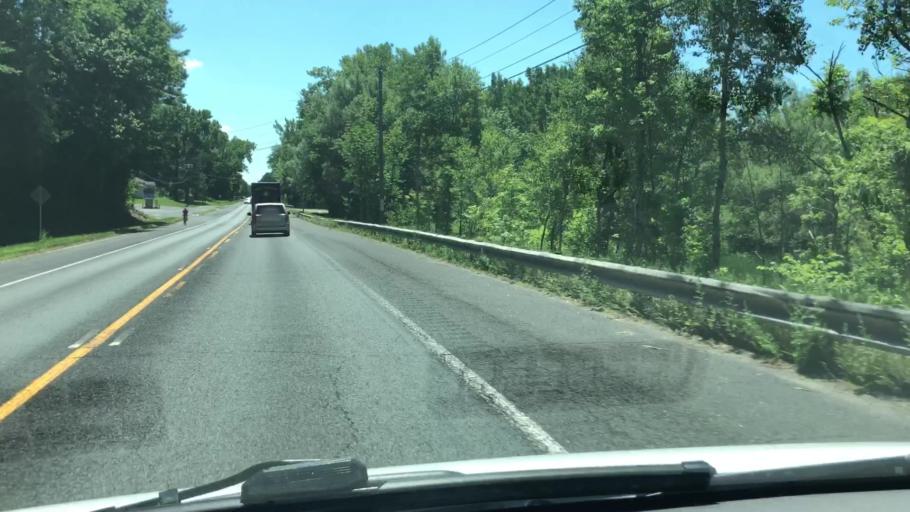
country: US
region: Massachusetts
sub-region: Berkshire County
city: Lanesborough
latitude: 42.5277
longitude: -73.1912
